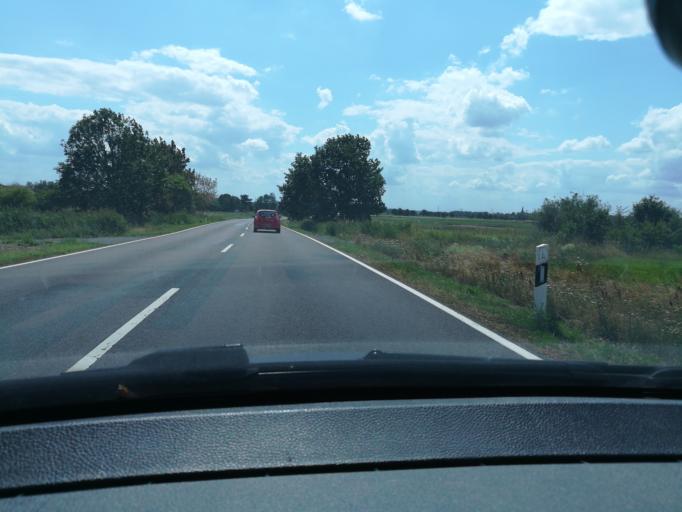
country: DE
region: Saxony-Anhalt
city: Zielitz
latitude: 52.2990
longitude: 11.6945
